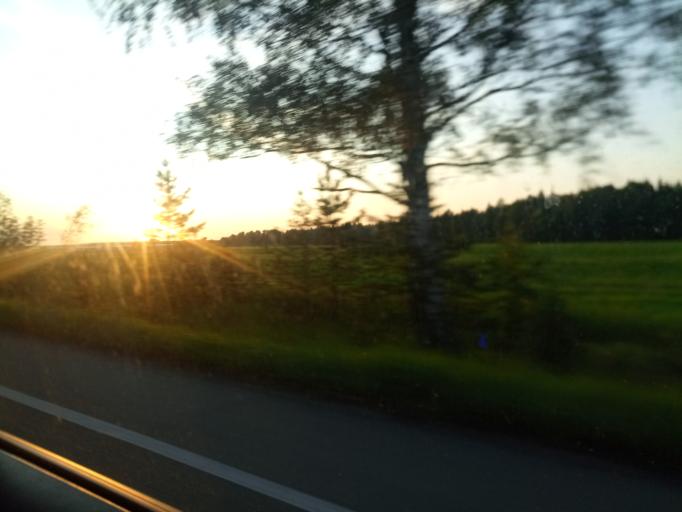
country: RU
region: Moskovskaya
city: Noginsk-9
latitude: 56.0467
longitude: 38.4980
